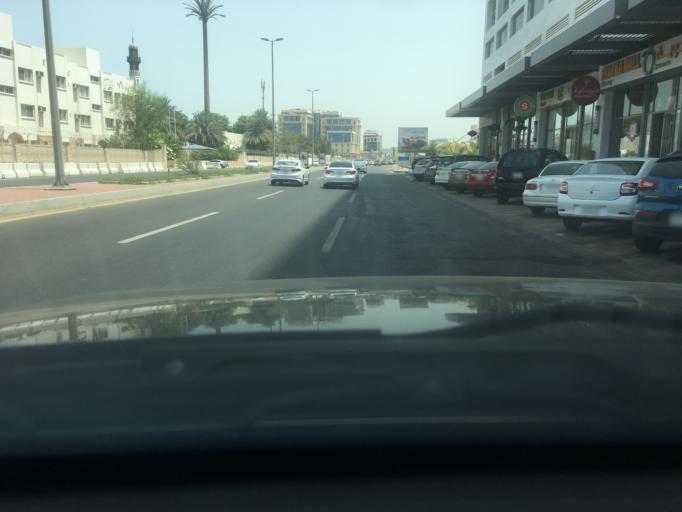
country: SA
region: Makkah
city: Jeddah
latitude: 21.5547
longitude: 39.1429
